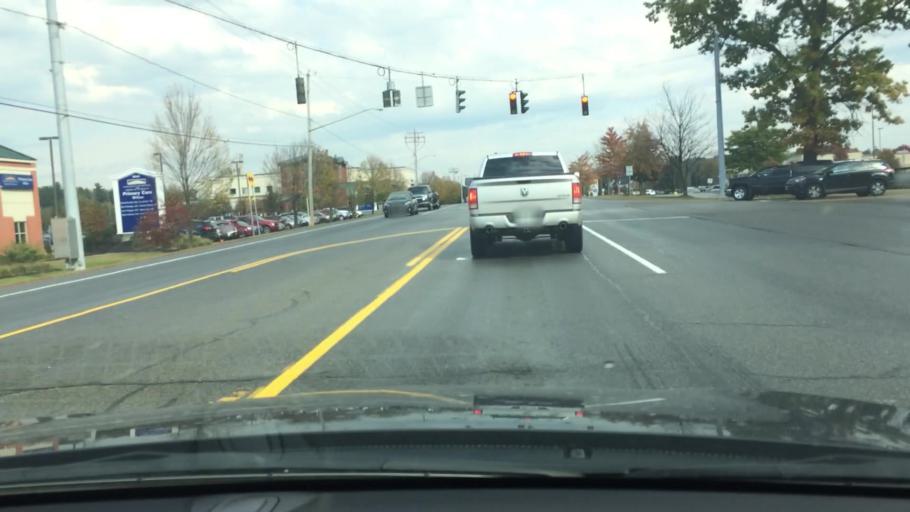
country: US
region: New York
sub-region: Saratoga County
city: Saratoga Springs
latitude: 43.1027
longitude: -73.7443
